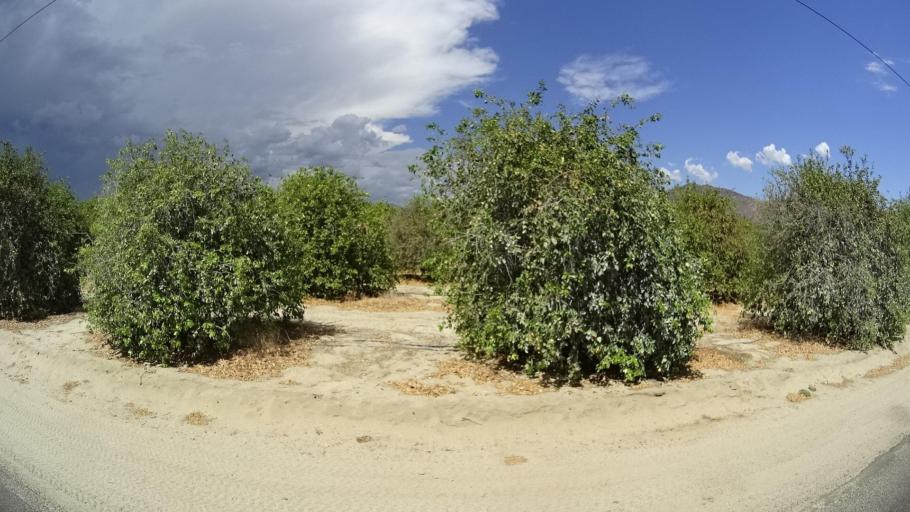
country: US
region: California
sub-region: San Diego County
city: Borrego Springs
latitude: 33.3006
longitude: -116.3642
